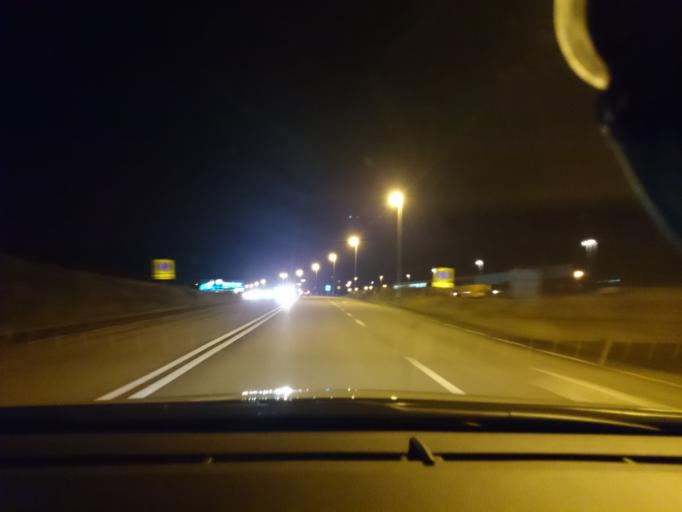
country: SE
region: Vaestra Goetaland
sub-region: Harryda Kommun
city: Landvetter
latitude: 57.6756
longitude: 12.3051
